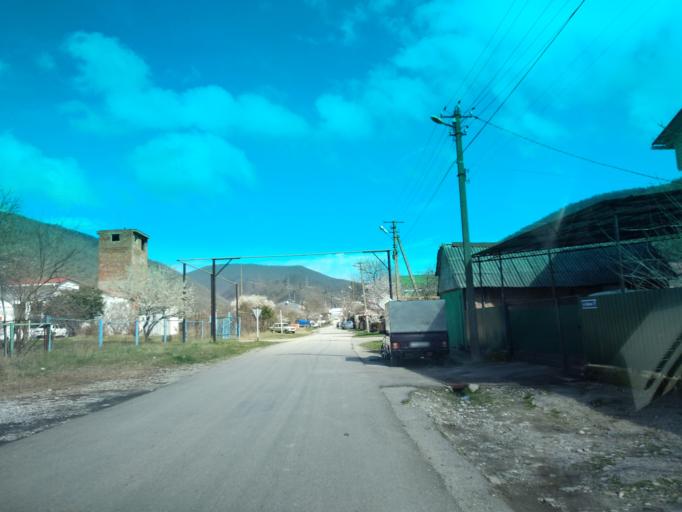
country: RU
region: Krasnodarskiy
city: Shepsi
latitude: 44.0504
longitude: 39.1606
